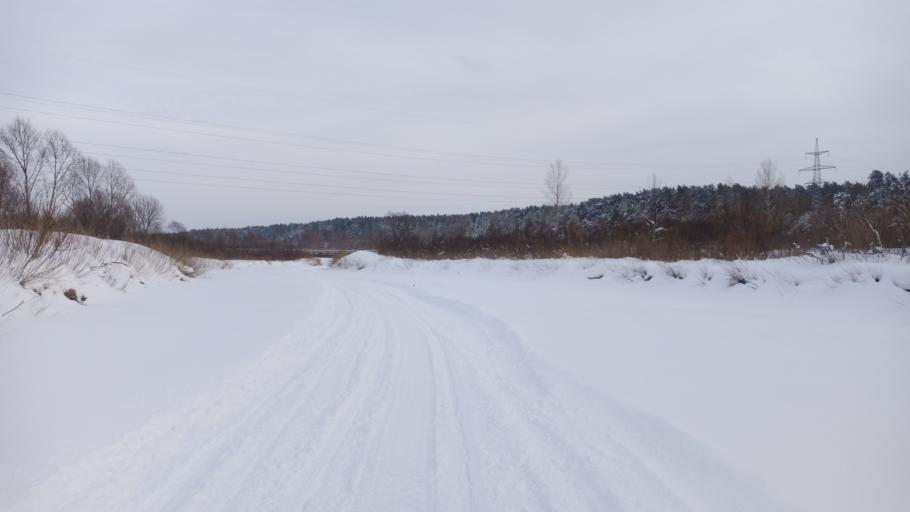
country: RU
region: Altai Krai
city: Yuzhnyy
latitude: 53.3071
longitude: 83.7115
